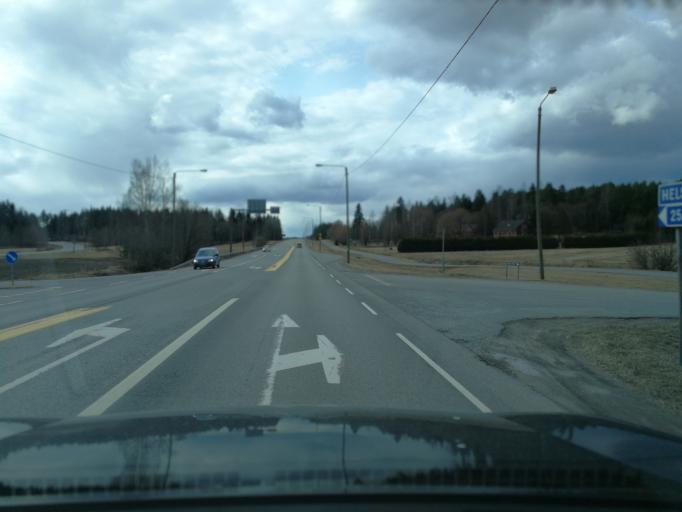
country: FI
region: Varsinais-Suomi
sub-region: Turku
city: Lieto
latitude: 60.4580
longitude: 22.4369
